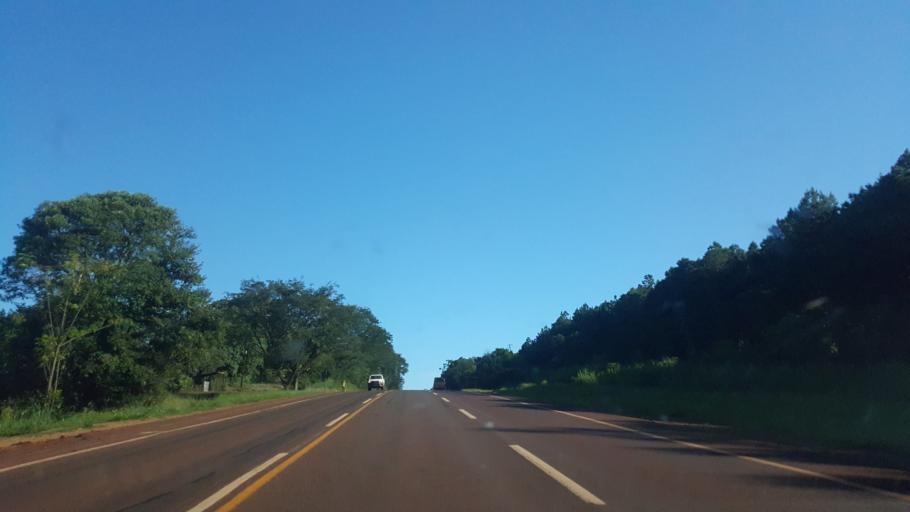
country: AR
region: Misiones
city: Puerto Esperanza
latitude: -26.1579
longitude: -54.5833
